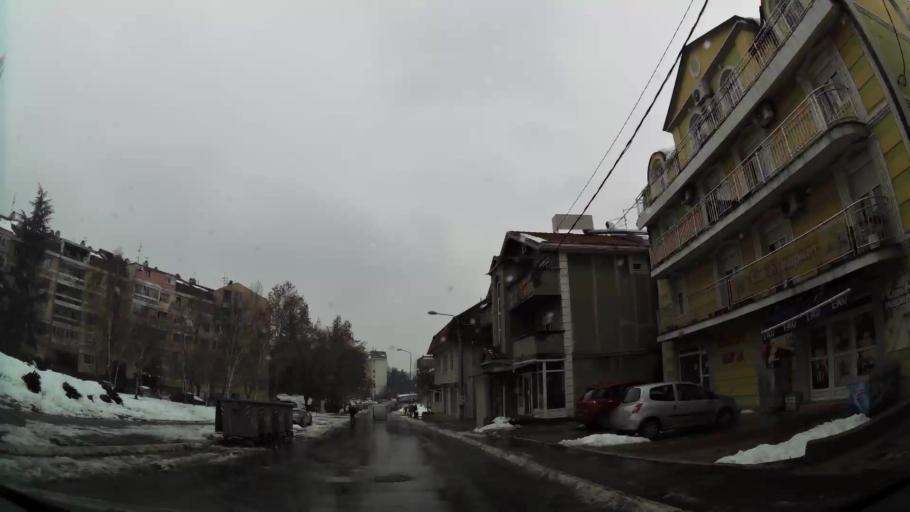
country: RS
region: Central Serbia
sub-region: Belgrade
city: Zemun
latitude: 44.8480
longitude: 20.3808
